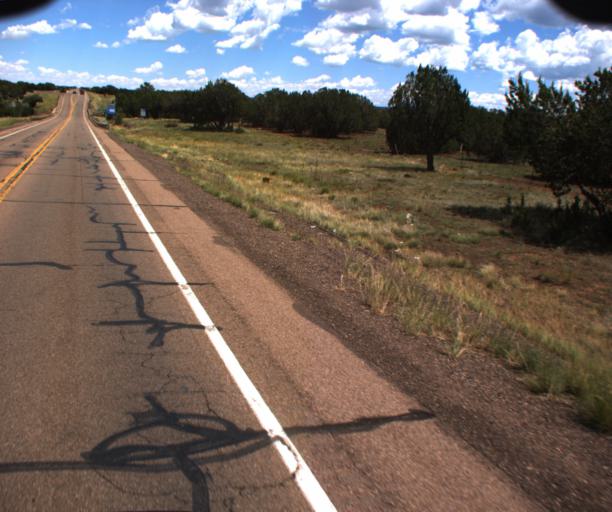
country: US
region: Arizona
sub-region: Navajo County
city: Show Low
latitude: 34.2680
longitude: -109.9394
